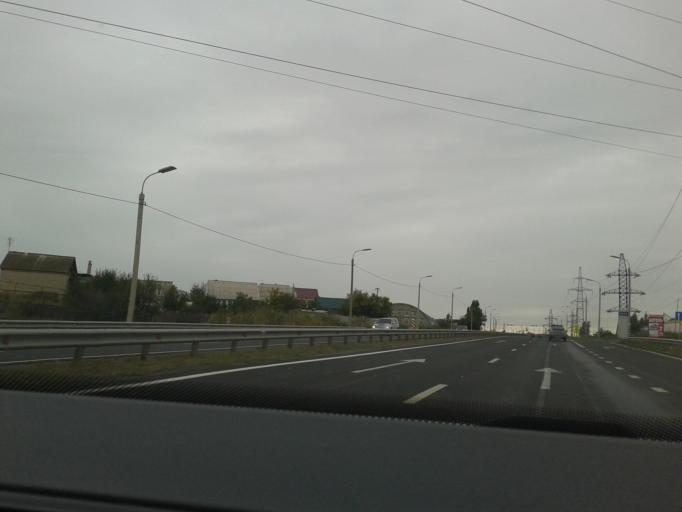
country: RU
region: Volgograd
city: Gorodishche
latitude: 48.7851
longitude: 44.4620
